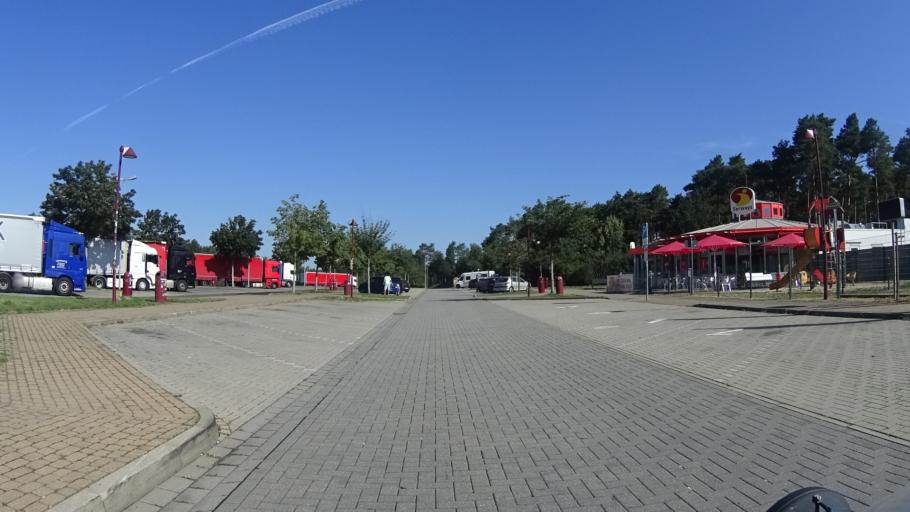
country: DE
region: Brandenburg
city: Bestensee
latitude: 52.2091
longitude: 13.6088
